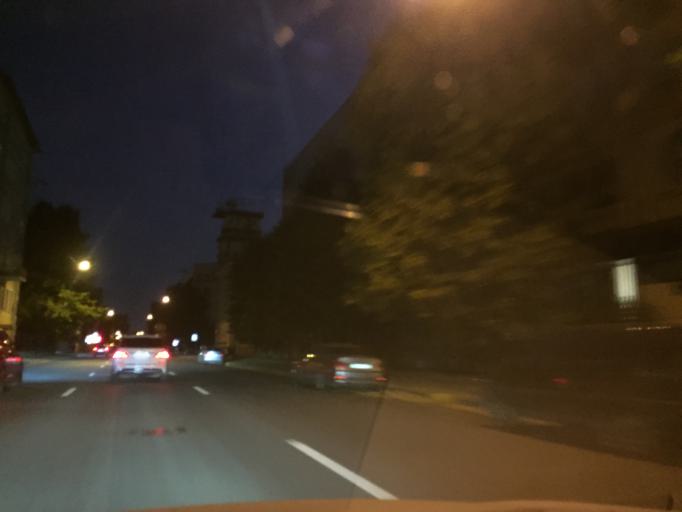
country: RU
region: St.-Petersburg
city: Centralniy
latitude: 59.9129
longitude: 30.3423
